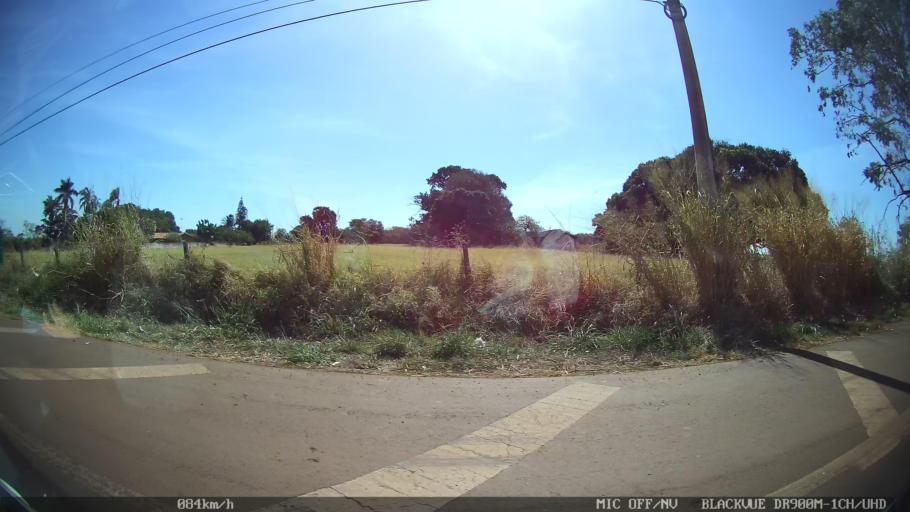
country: BR
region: Sao Paulo
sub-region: Barretos
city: Barretos
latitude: -20.5289
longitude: -48.5935
